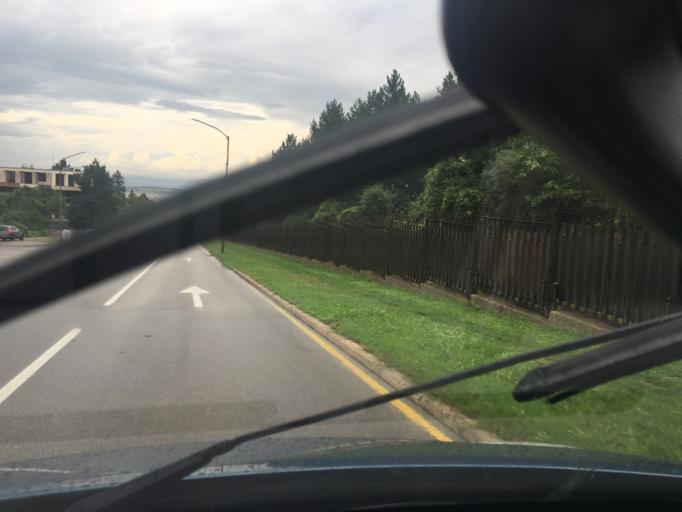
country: BG
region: Sofia-Capital
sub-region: Stolichna Obshtina
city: Sofia
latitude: 42.6518
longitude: 23.2662
